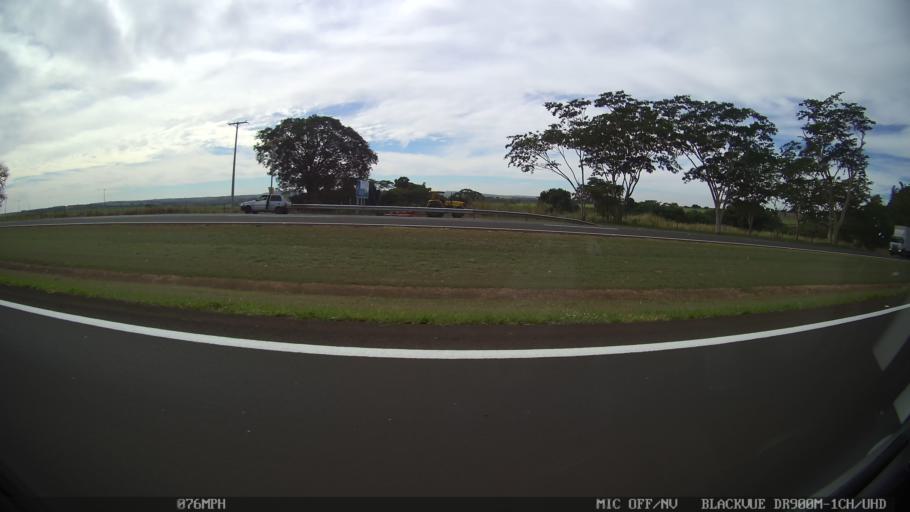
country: BR
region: Sao Paulo
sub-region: Taquaritinga
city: Taquaritinga
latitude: -21.4609
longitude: -48.6199
